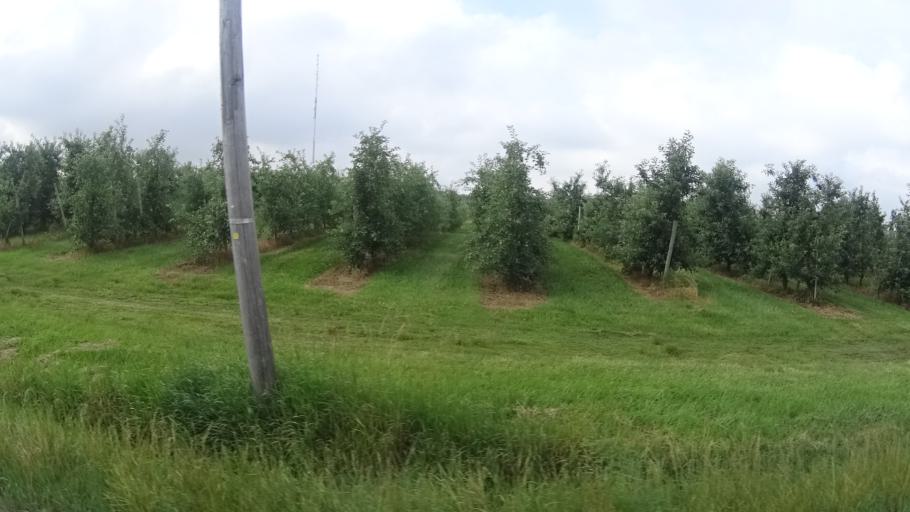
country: US
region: Ohio
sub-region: Huron County
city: Wakeman
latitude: 41.3050
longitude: -82.4890
